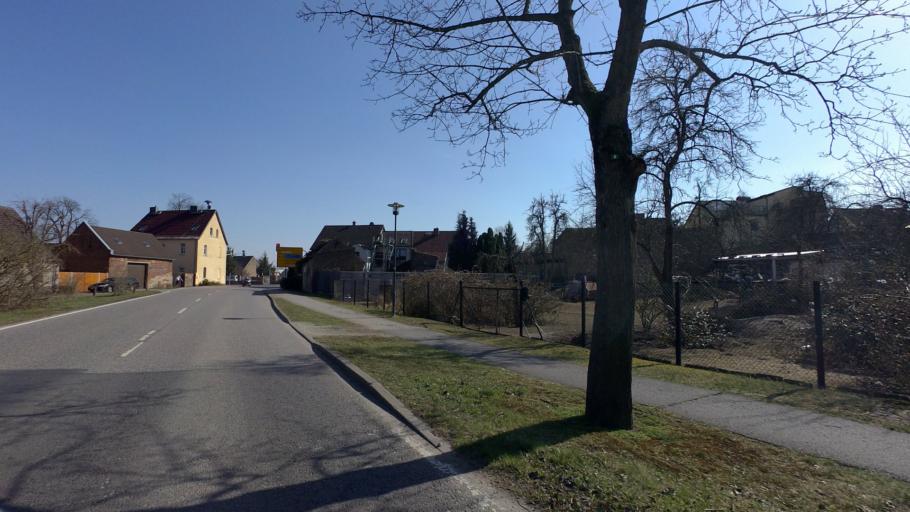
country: DE
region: Brandenburg
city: Leegebruch
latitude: 52.7496
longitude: 13.1714
